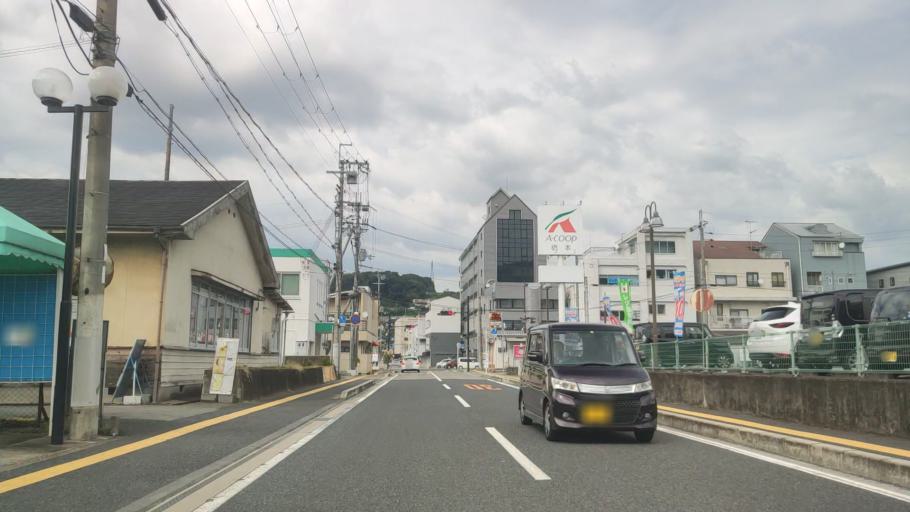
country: JP
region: Wakayama
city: Hashimoto
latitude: 34.3134
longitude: 135.6049
